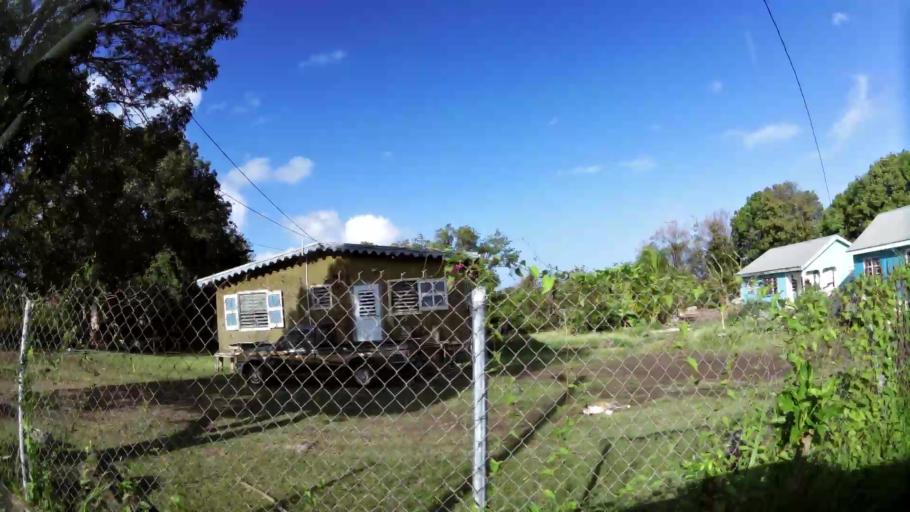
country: KN
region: Saint Paul Charlestown
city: Charlestown
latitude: 17.1445
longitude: -62.6267
